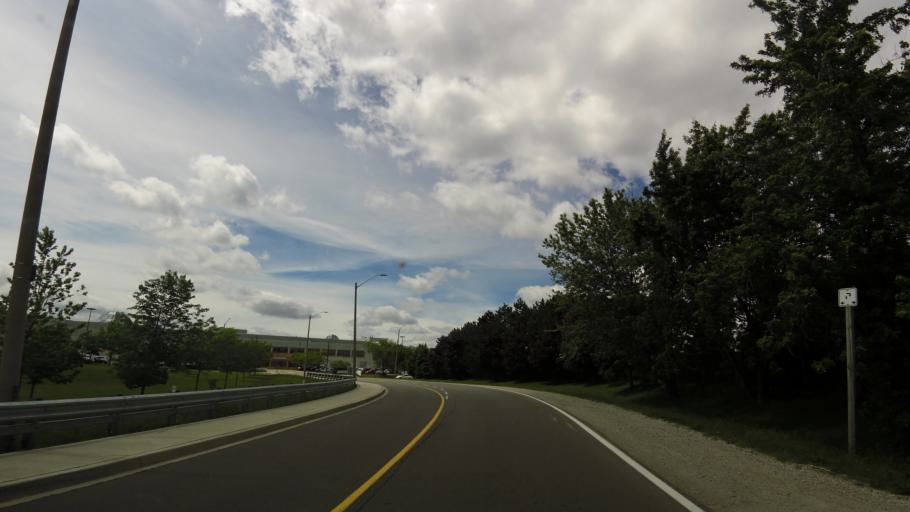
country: CA
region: Ontario
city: Mississauga
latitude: 43.5305
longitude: -79.6503
